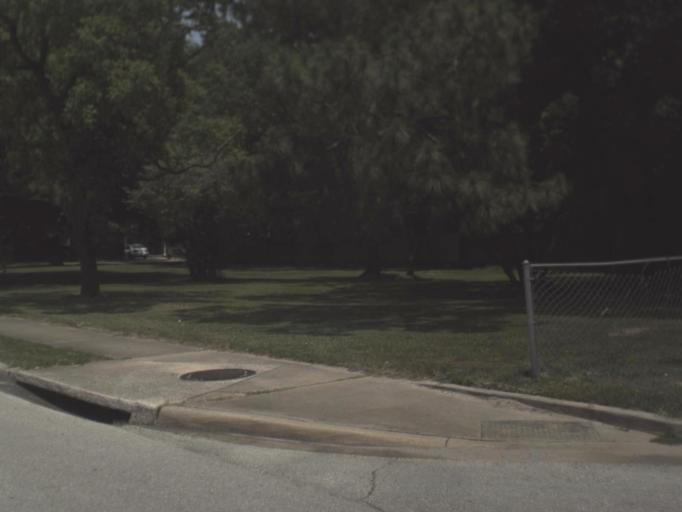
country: US
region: Florida
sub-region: Duval County
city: Jacksonville
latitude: 30.3389
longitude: -81.7310
